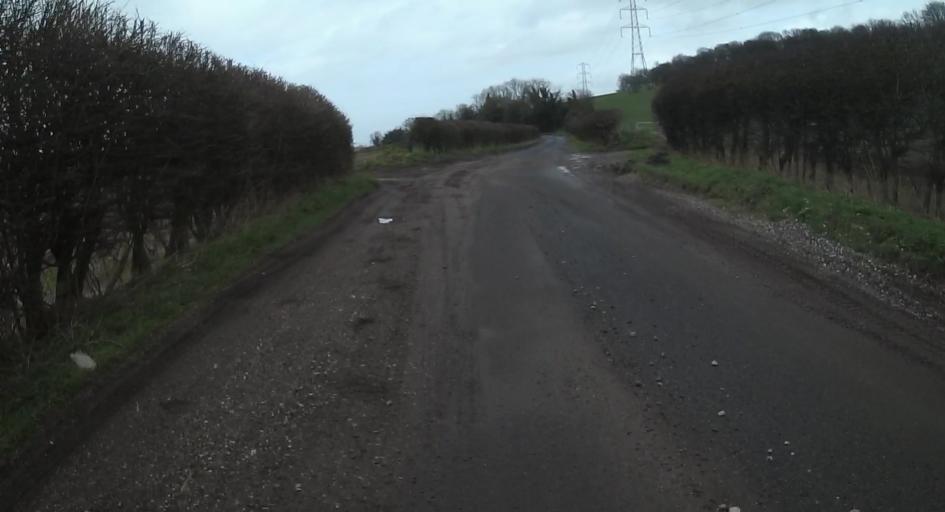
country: GB
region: England
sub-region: Hampshire
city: Kingsclere
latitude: 51.3054
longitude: -1.2174
